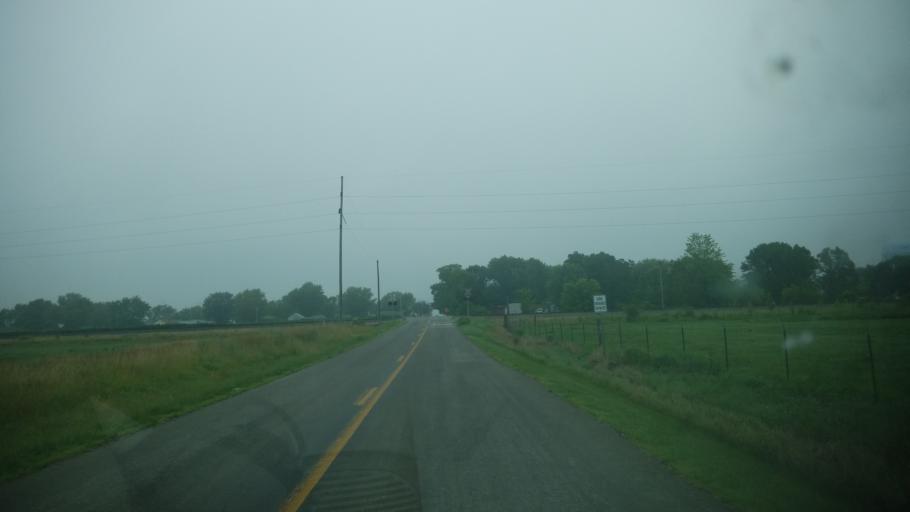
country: US
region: Missouri
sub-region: Audrain County
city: Vandalia
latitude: 39.3418
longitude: -91.3449
